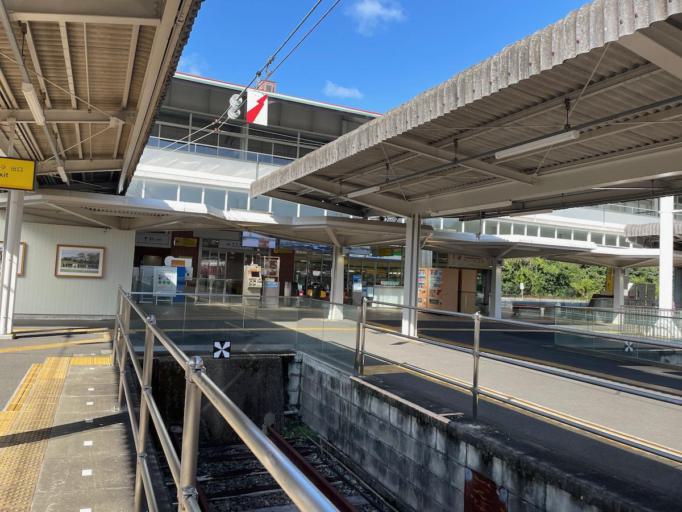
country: JP
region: Mie
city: Toba
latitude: 34.3084
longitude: 136.8189
